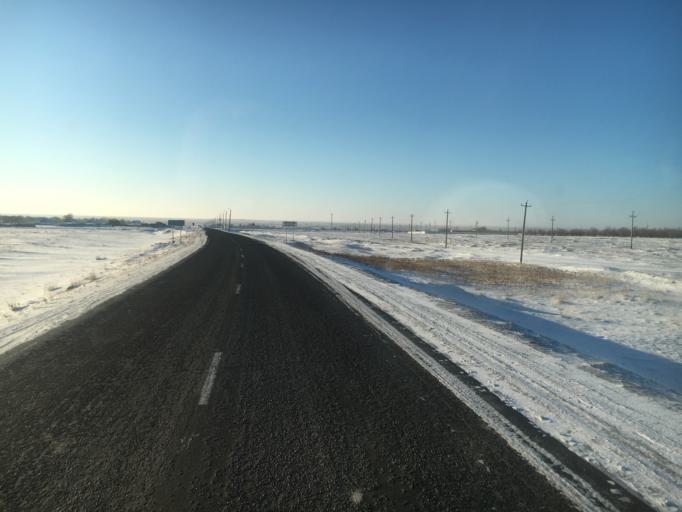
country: KZ
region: Aqtoebe
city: Khromtau
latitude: 50.1268
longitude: 59.1140
